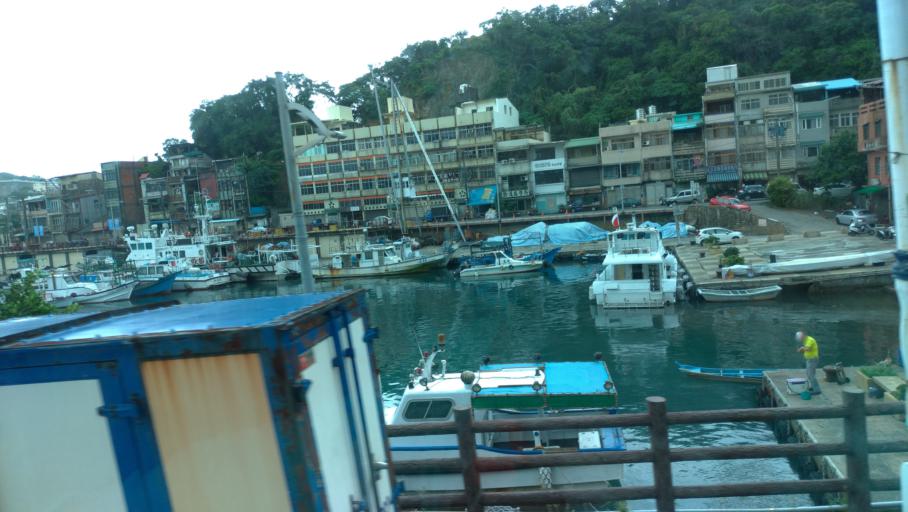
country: TW
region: Taiwan
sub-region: Keelung
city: Keelung
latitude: 25.1521
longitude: 121.7697
